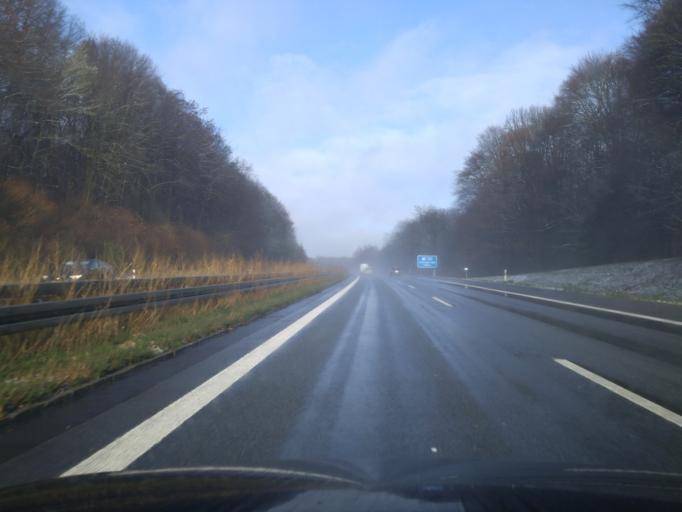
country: DE
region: Bavaria
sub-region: Regierungsbezirk Unterfranken
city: Unterpleichfeld
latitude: 49.8959
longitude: 10.0014
